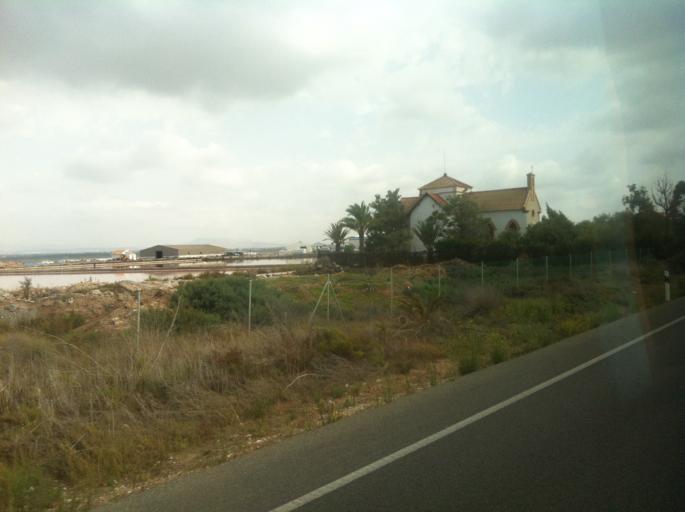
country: ES
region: Valencia
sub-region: Provincia de Alicante
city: Santa Pola
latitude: 38.1895
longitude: -0.5976
